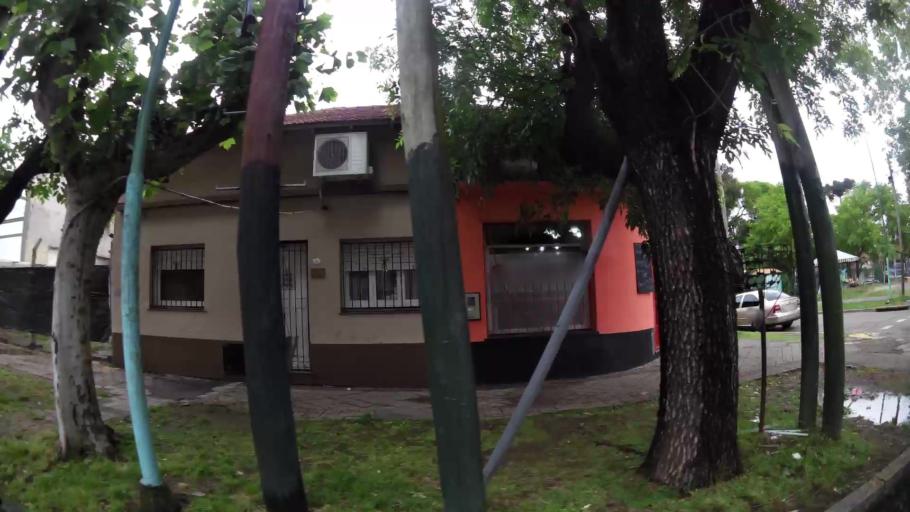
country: AR
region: Buenos Aires
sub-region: Partido de Lomas de Zamora
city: Lomas de Zamora
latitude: -34.7621
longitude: -58.3894
